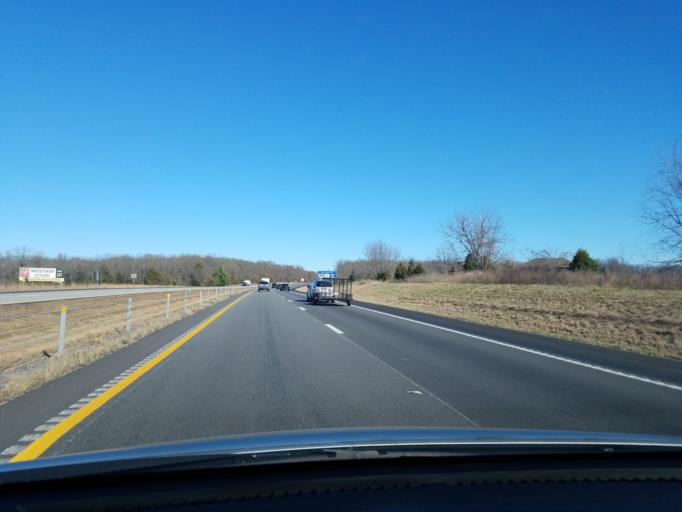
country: US
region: Missouri
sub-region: Webster County
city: Marshfield
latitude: 37.3236
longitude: -92.9585
